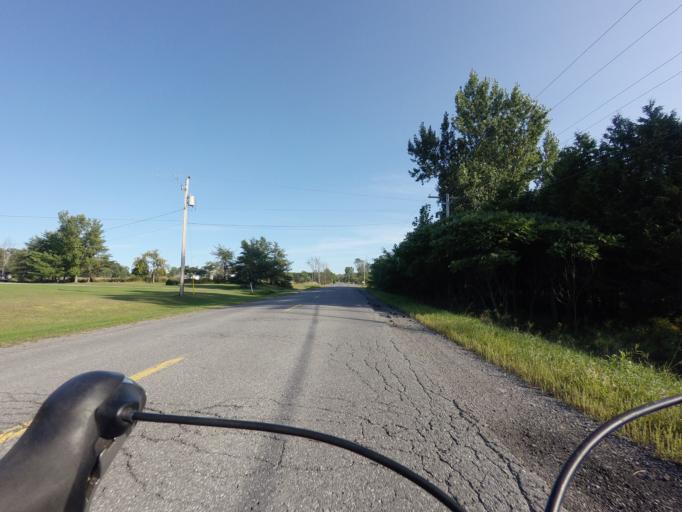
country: CA
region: Ontario
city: Bells Corners
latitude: 45.4651
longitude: -76.0264
